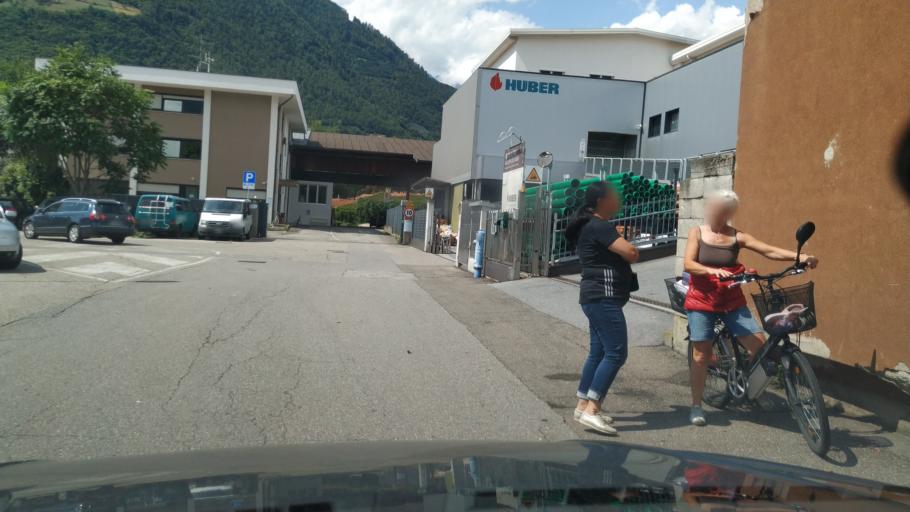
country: IT
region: Trentino-Alto Adige
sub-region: Bolzano
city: Marlengo
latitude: 46.6533
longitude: 11.1559
